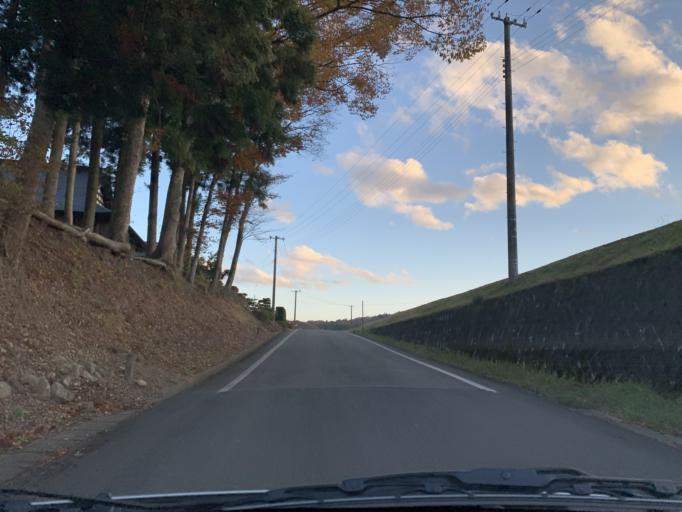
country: JP
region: Iwate
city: Mizusawa
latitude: 39.0399
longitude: 141.0551
